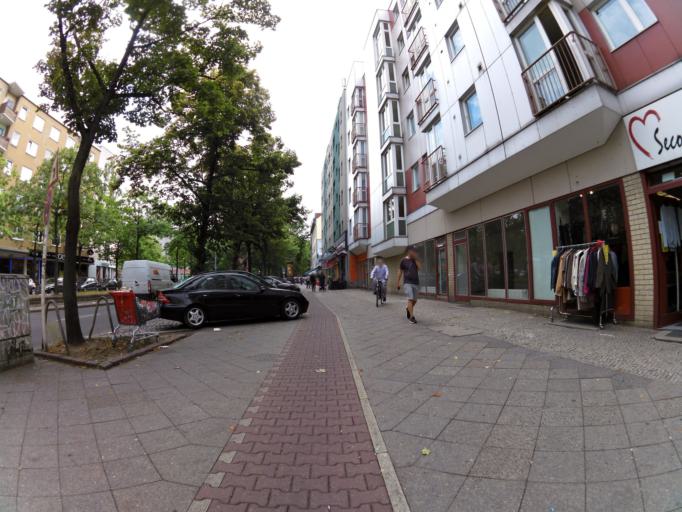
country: DE
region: Berlin
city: Wedding Bezirk
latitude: 52.5460
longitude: 13.3692
